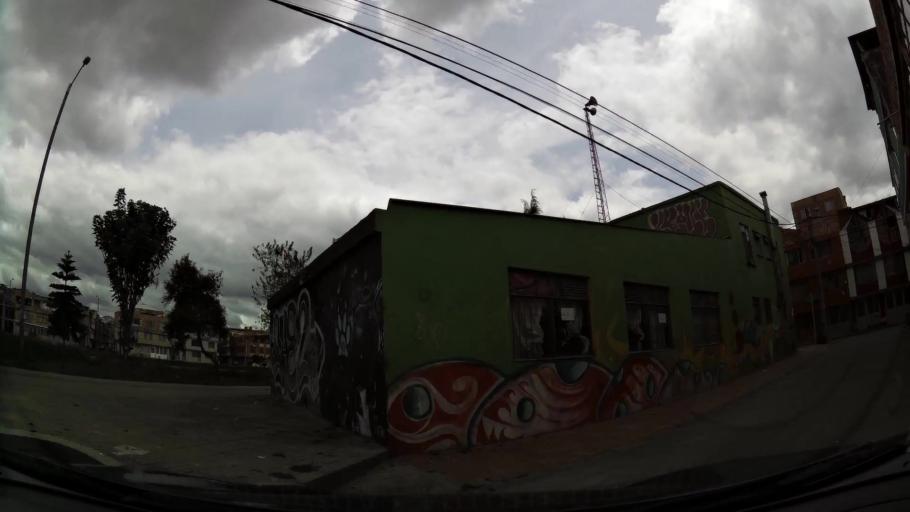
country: CO
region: Cundinamarca
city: Funza
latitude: 4.7025
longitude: -74.1277
